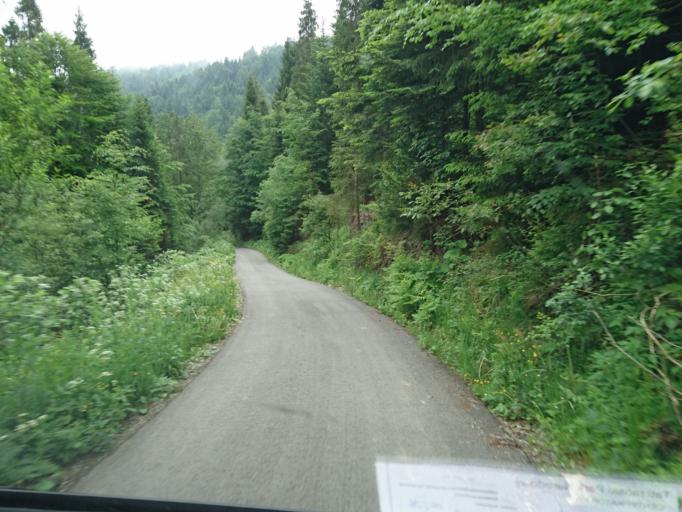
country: PL
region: Lesser Poland Voivodeship
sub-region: Powiat limanowski
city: Lubomierz
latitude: 49.5351
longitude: 20.2098
